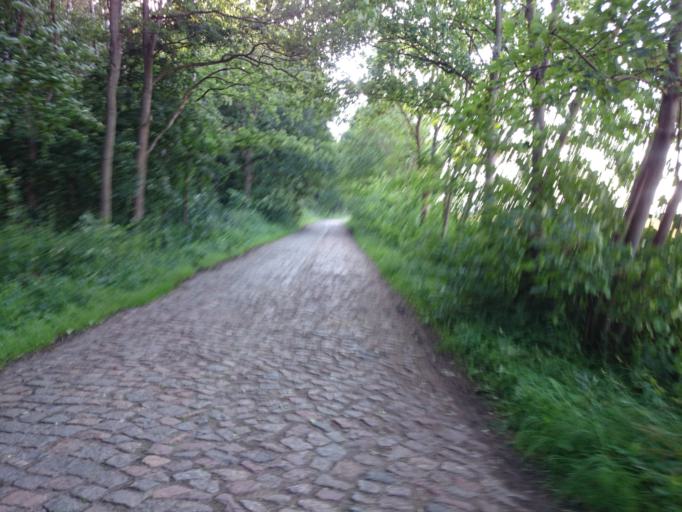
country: DE
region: Mecklenburg-Vorpommern
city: Broderstorf
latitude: 54.0610
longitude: 12.3550
